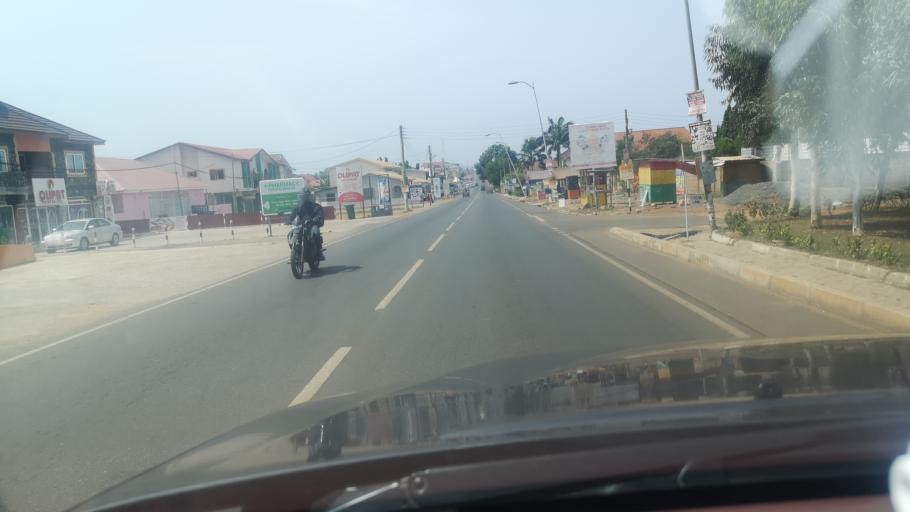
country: GH
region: Greater Accra
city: Nungua
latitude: 5.6416
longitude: -0.0763
